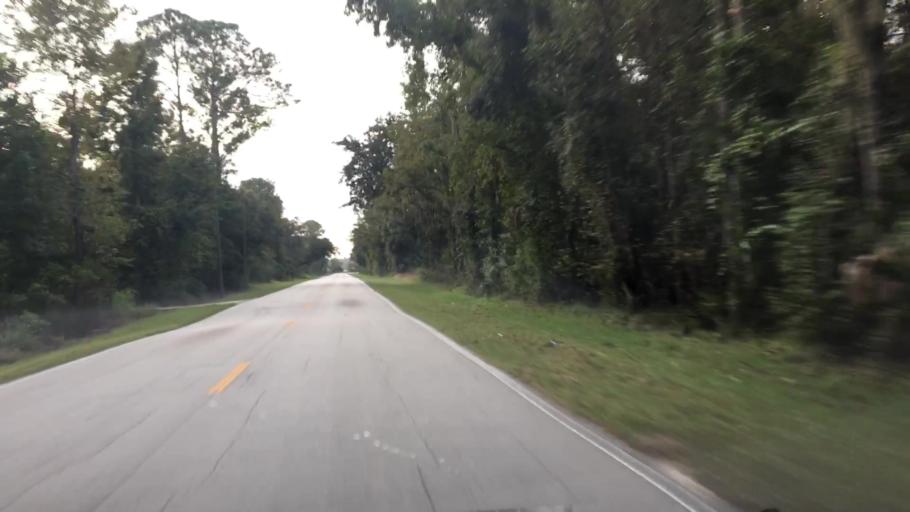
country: US
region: Florida
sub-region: Seminole County
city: Midway
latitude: 28.8437
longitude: -81.1984
